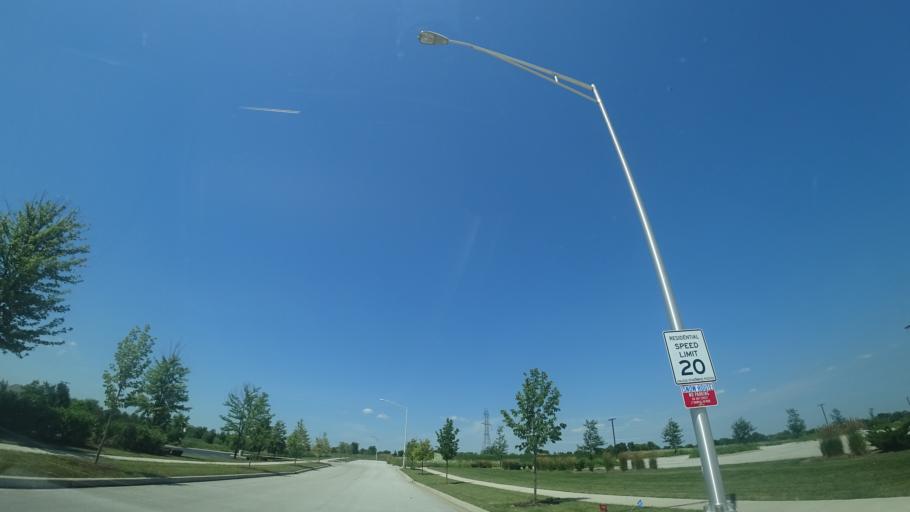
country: US
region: Illinois
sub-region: Will County
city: Mokena
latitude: 41.5577
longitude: -87.8840
